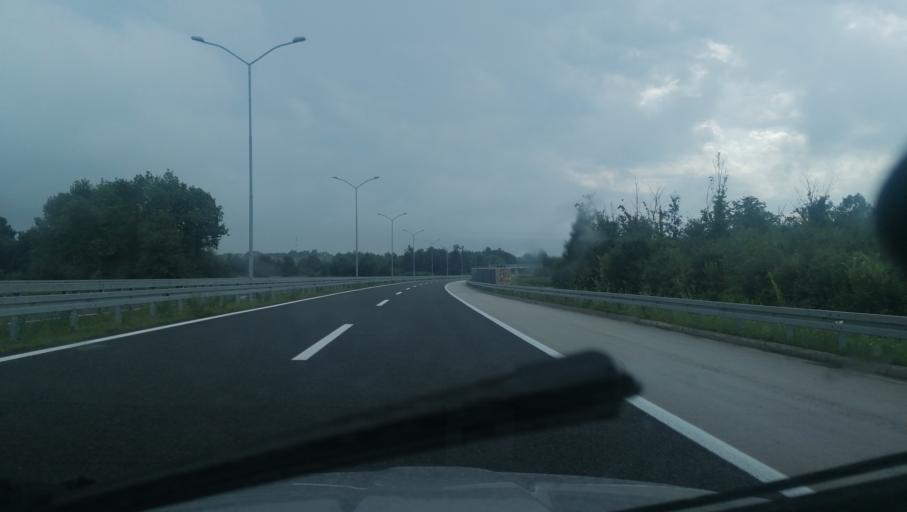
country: BA
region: Republika Srpska
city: Maglajani
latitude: 44.8973
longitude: 17.3593
